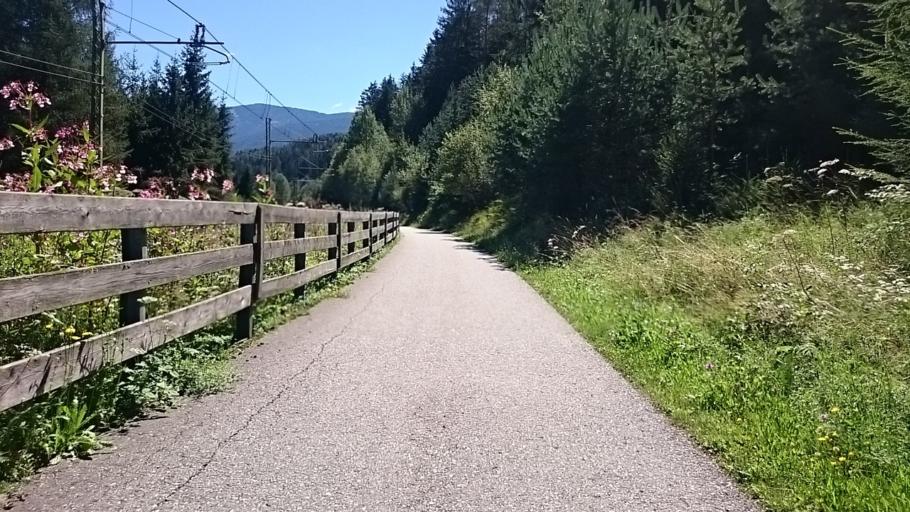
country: IT
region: Trentino-Alto Adige
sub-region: Bolzano
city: Chienes
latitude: 46.7901
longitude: 11.8574
